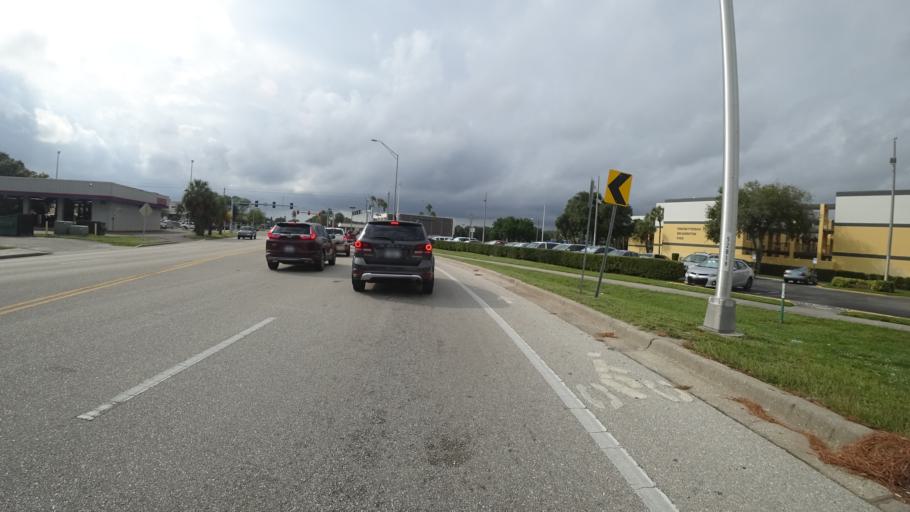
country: US
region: Florida
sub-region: Manatee County
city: Bayshore Gardens
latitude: 27.4312
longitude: -82.5744
